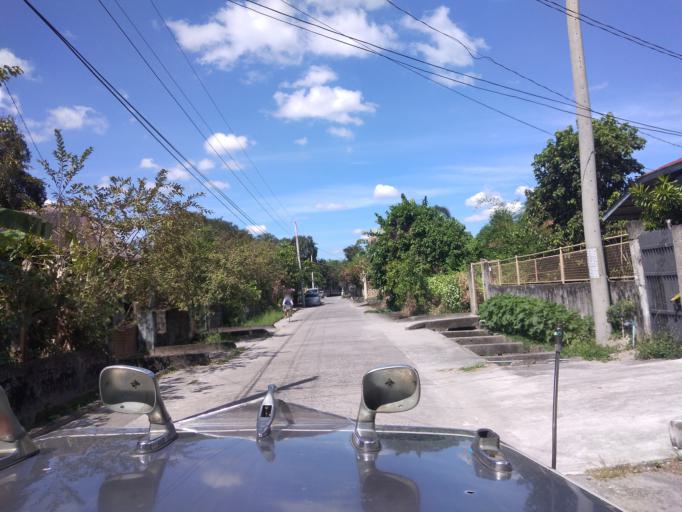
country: PH
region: Central Luzon
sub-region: Province of Pampanga
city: Santa Rita
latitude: 15.0054
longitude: 120.5962
